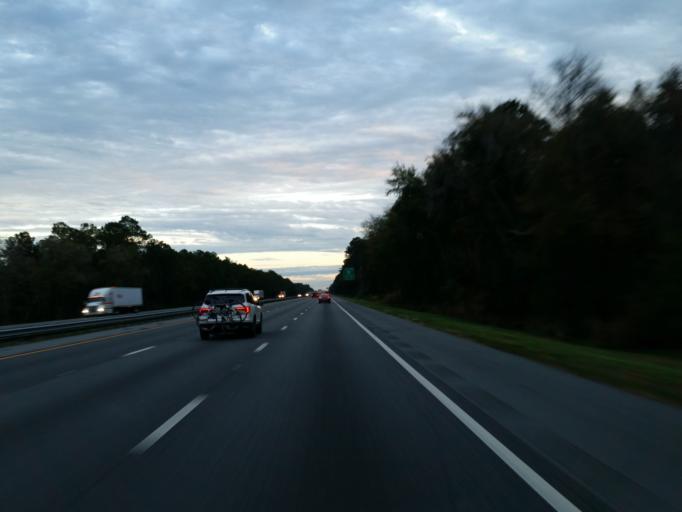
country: US
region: Florida
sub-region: Hamilton County
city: Jasper
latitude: 30.4659
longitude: -82.9616
